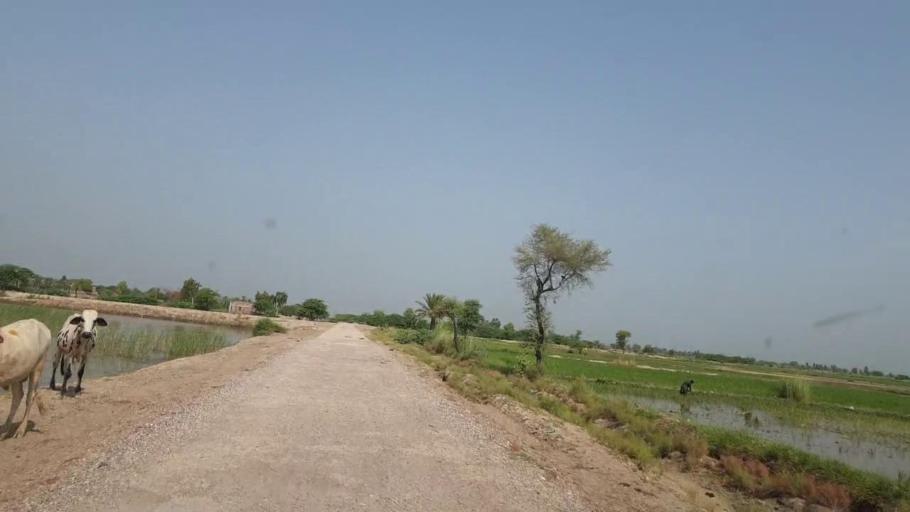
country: PK
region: Sindh
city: Lakhi
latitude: 27.8269
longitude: 68.6894
